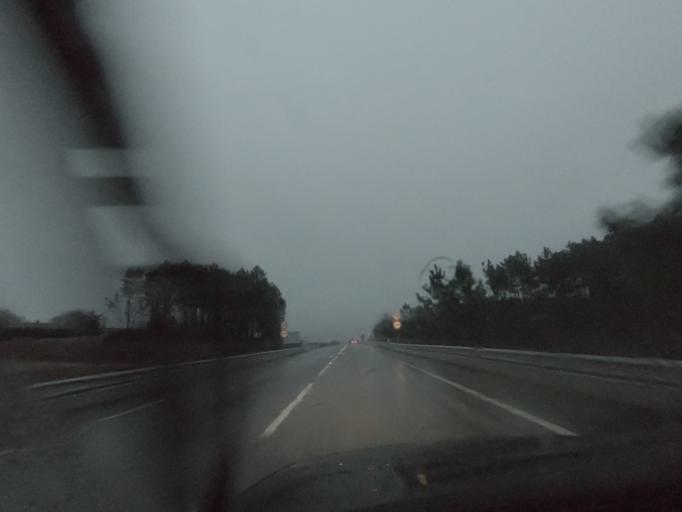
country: PT
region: Vila Real
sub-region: Sabrosa
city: Vilela
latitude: 41.2636
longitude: -7.6248
